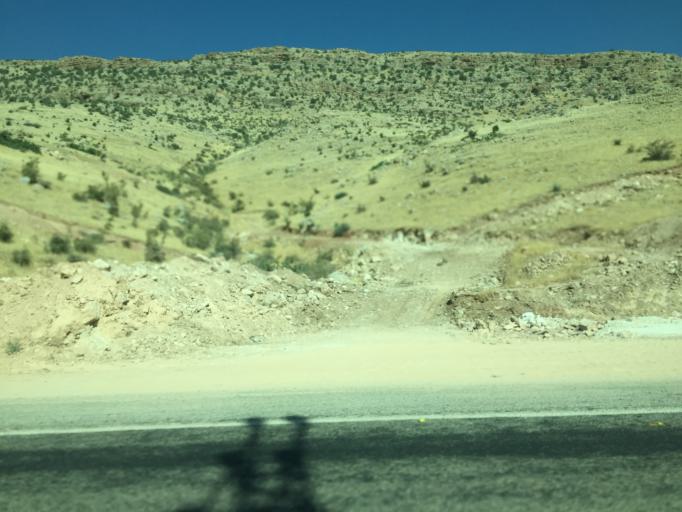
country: TR
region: Batman
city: Hasankeyf
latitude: 37.6912
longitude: 41.4566
